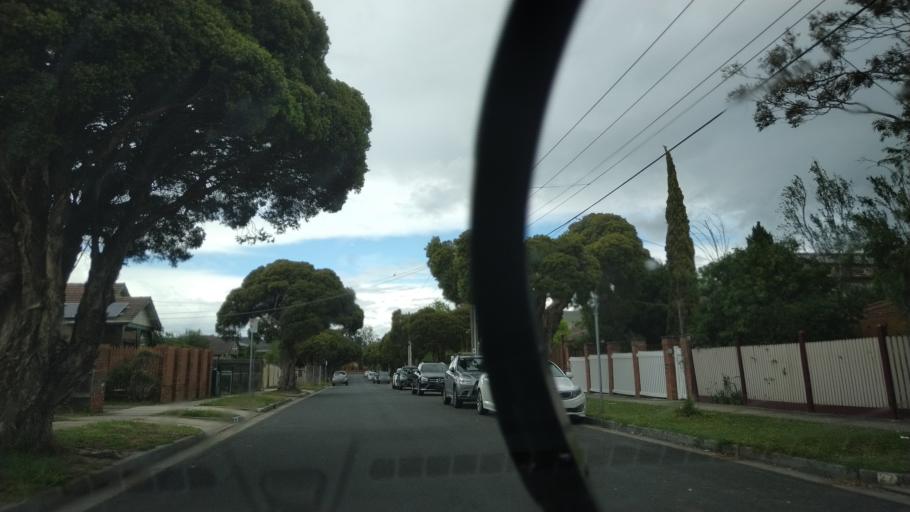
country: AU
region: Victoria
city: Ormond
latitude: -37.9059
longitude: 145.0406
